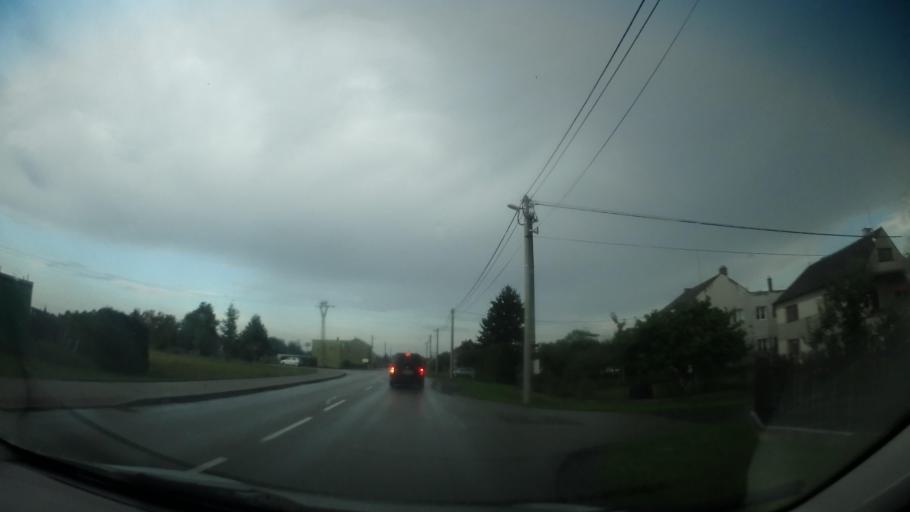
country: CZ
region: Olomoucky
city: Cervenka
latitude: 49.7127
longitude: 17.1022
